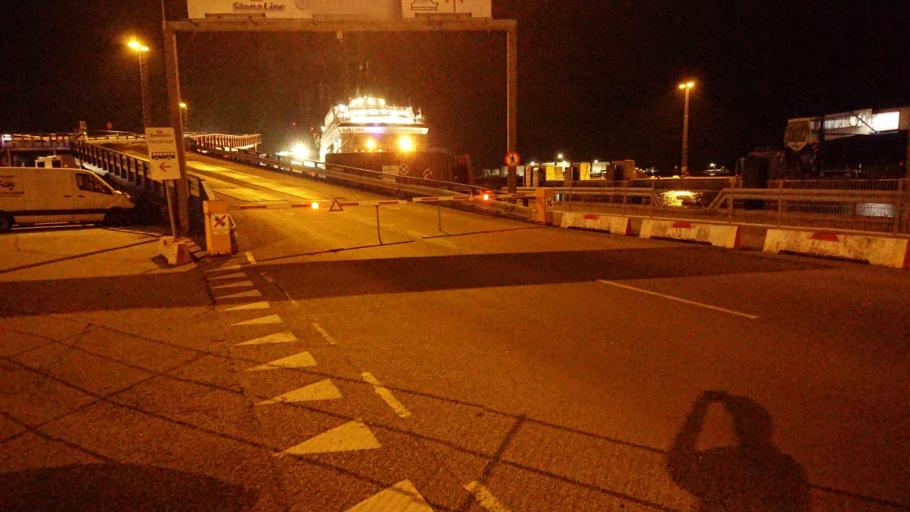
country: DK
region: North Denmark
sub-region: Frederikshavn Kommune
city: Frederikshavn
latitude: 57.4343
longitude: 10.5440
